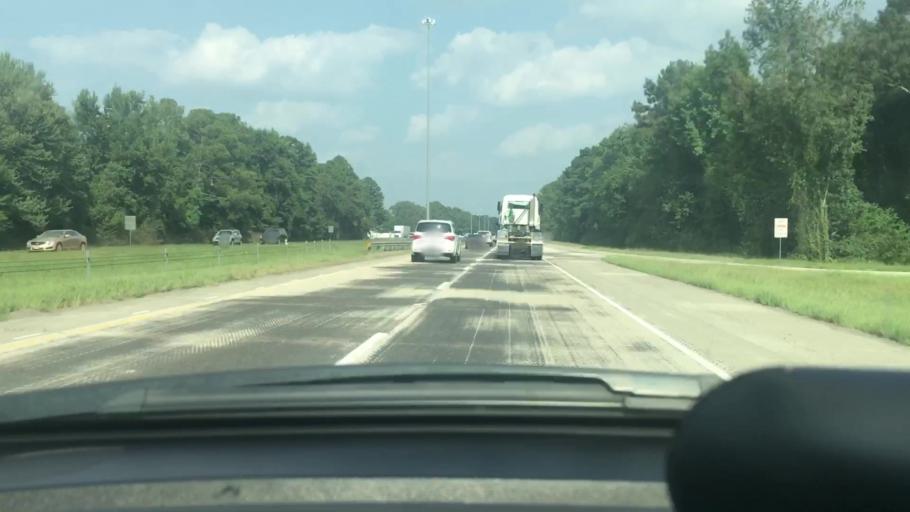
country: US
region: Louisiana
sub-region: Tangipahoa Parish
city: Hammond
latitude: 30.4793
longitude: -90.5196
